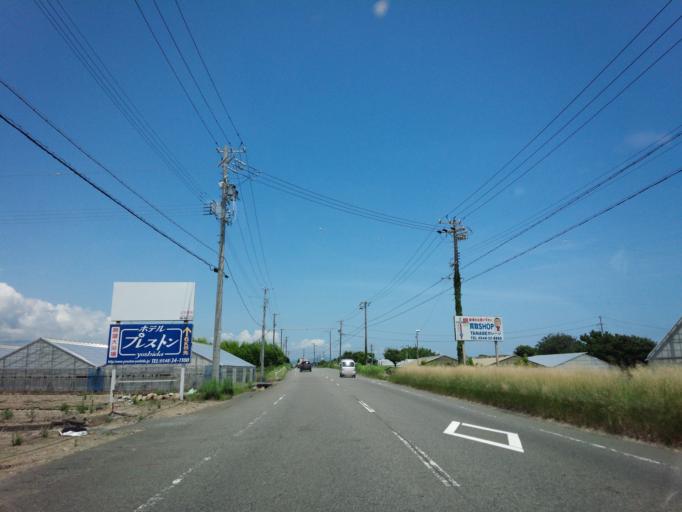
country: JP
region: Shizuoka
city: Sagara
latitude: 34.7198
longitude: 138.2182
